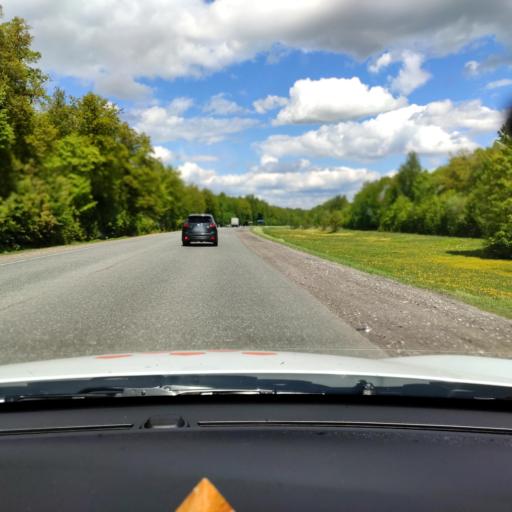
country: RU
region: Tatarstan
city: Verkhniy Uslon
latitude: 55.6860
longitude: 48.8717
